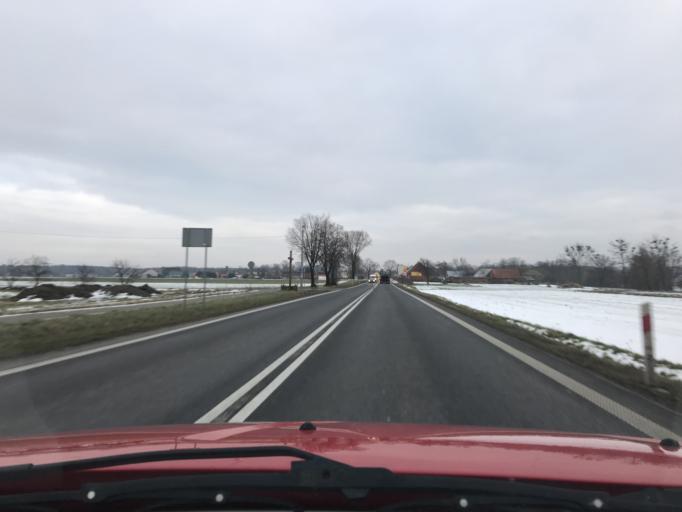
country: PL
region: Greater Poland Voivodeship
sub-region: Powiat pleszewski
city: Pleszew
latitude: 51.8874
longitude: 17.8518
